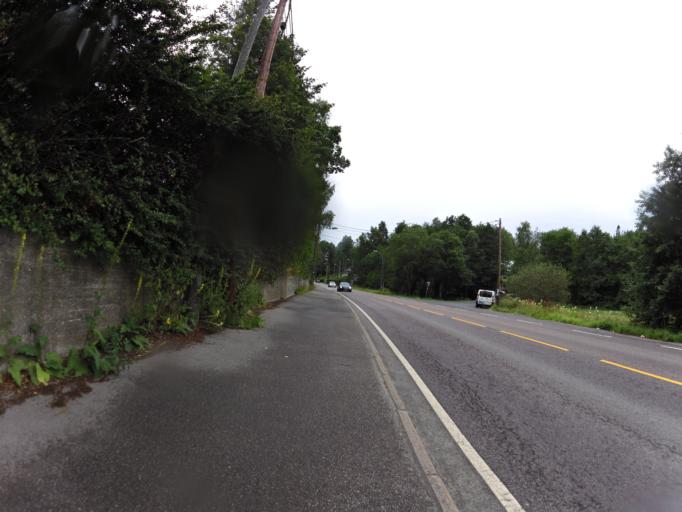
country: NO
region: Ostfold
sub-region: Moss
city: Moss
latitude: 59.4696
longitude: 10.6900
